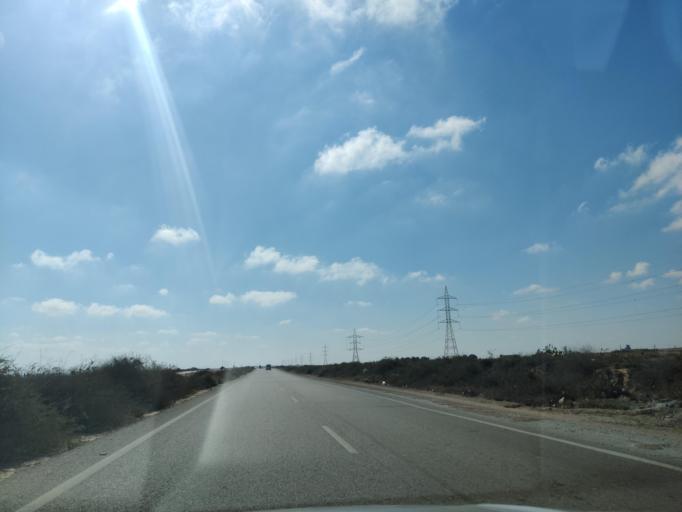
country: EG
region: Muhafazat Matruh
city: Al `Alamayn
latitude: 31.0492
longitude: 28.3299
